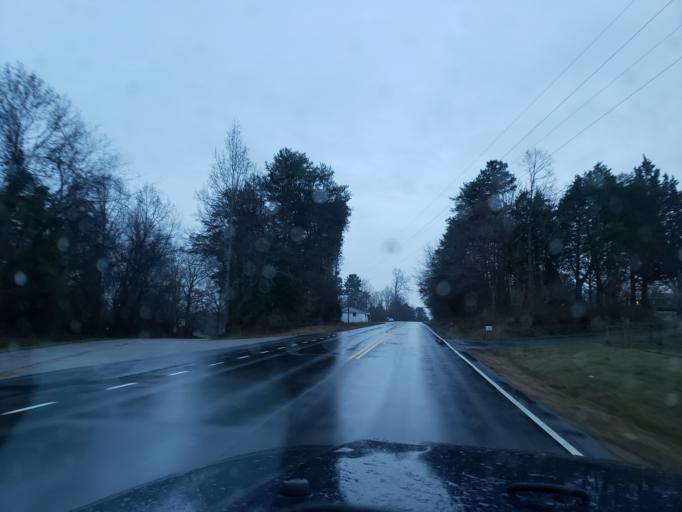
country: US
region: South Carolina
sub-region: Cherokee County
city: Blacksburg
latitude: 35.1511
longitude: -81.4517
